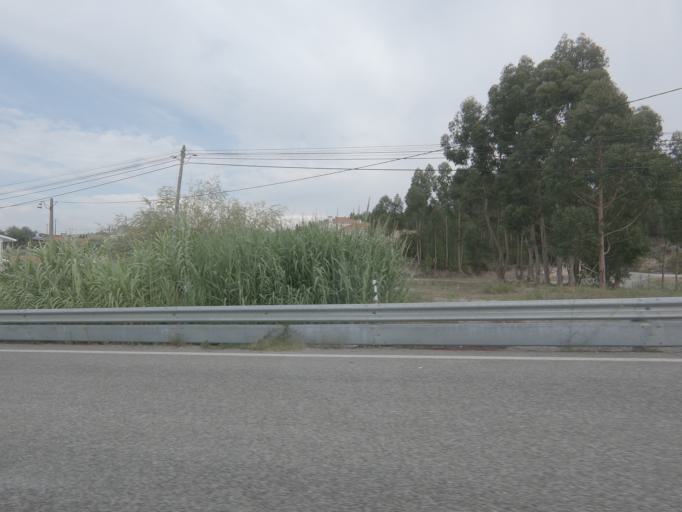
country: PT
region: Coimbra
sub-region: Condeixa-A-Nova
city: Condeixa-a-Nova
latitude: 40.1457
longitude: -8.4643
